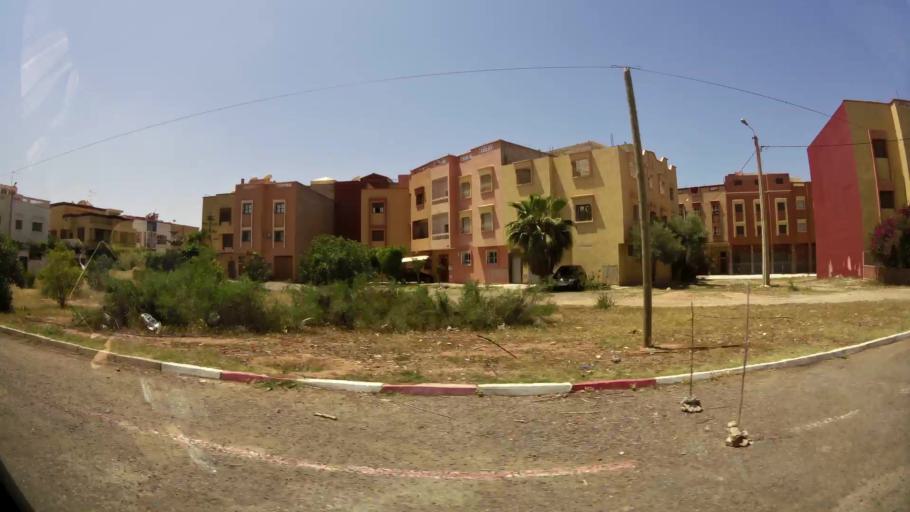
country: MA
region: Souss-Massa-Draa
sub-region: Inezgane-Ait Mellou
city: Inezgane
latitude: 30.3463
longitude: -9.4823
